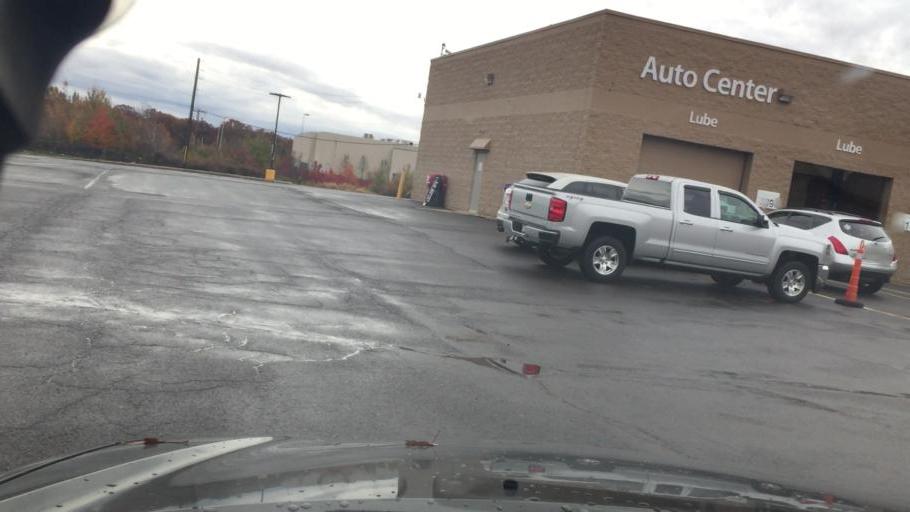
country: US
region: Pennsylvania
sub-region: Luzerne County
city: West Hazleton
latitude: 40.9868
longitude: -76.0112
